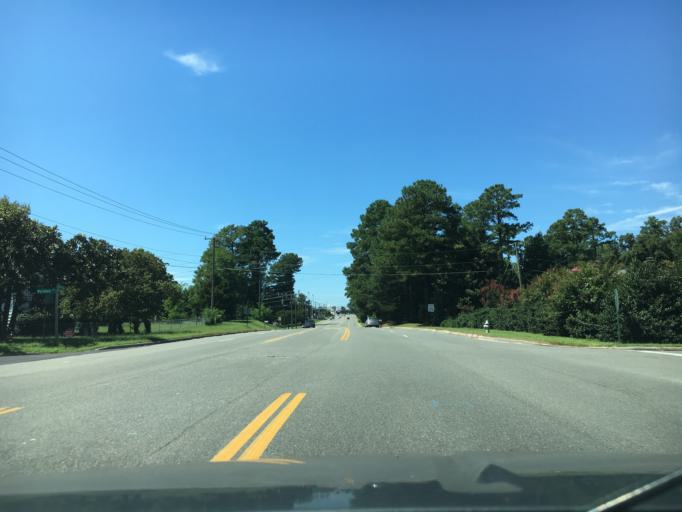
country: US
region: Virginia
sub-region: Henrico County
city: Tuckahoe
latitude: 37.6010
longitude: -77.5514
